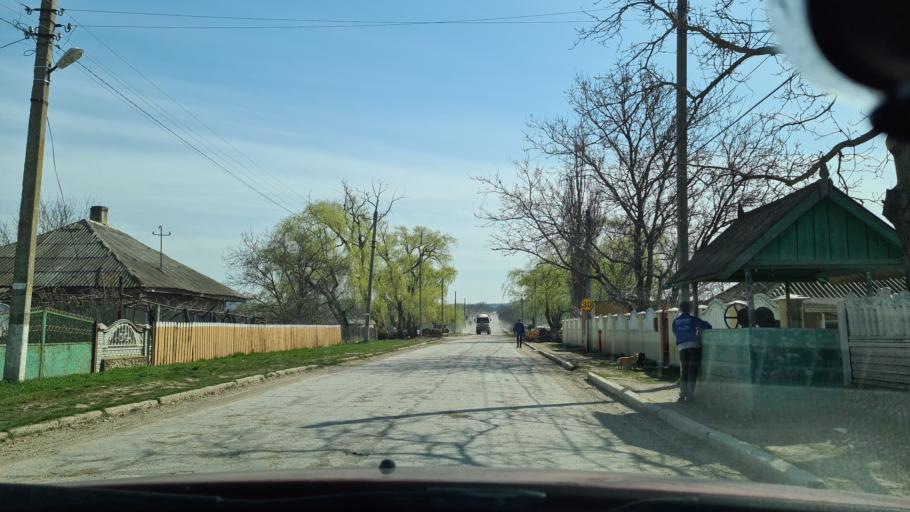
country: MD
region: Ungheni
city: Ungheni
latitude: 47.2690
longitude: 27.9345
